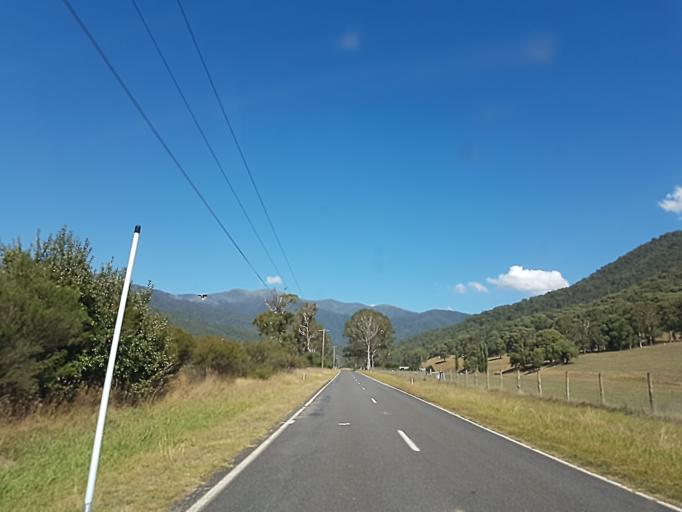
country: AU
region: Victoria
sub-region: Alpine
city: Mount Beauty
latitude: -36.8240
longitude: 147.0680
